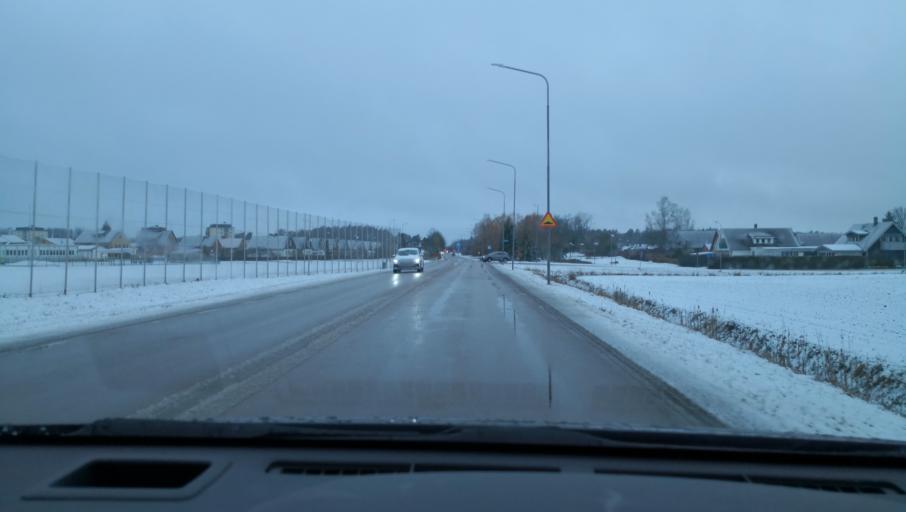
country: SE
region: Vaestmanland
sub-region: Kopings Kommun
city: Koping
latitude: 59.5158
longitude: 16.0133
